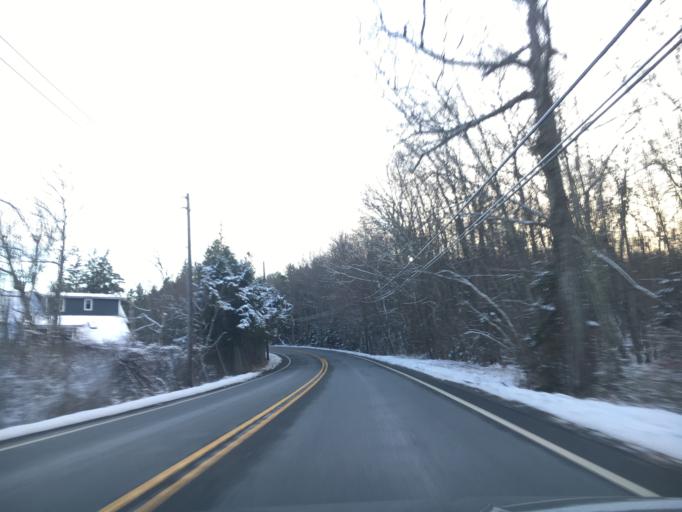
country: US
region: Pennsylvania
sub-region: Pike County
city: Hemlock Farms
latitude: 41.2499
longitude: -75.0692
